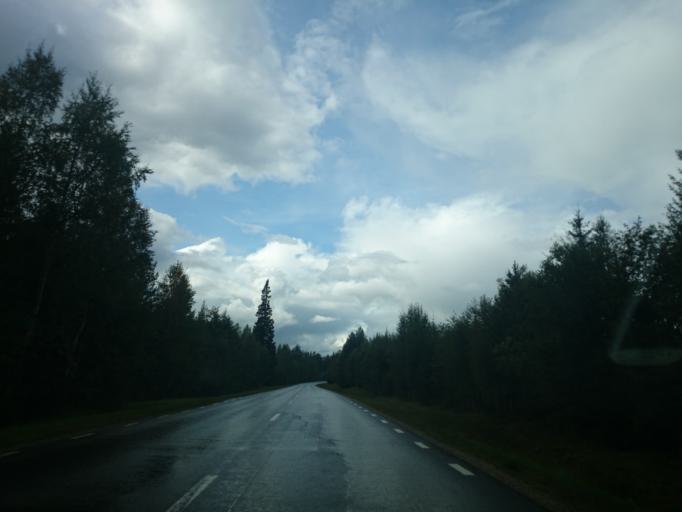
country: SE
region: Jaemtland
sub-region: Bergs Kommun
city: Hoverberg
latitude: 62.4953
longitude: 14.5925
